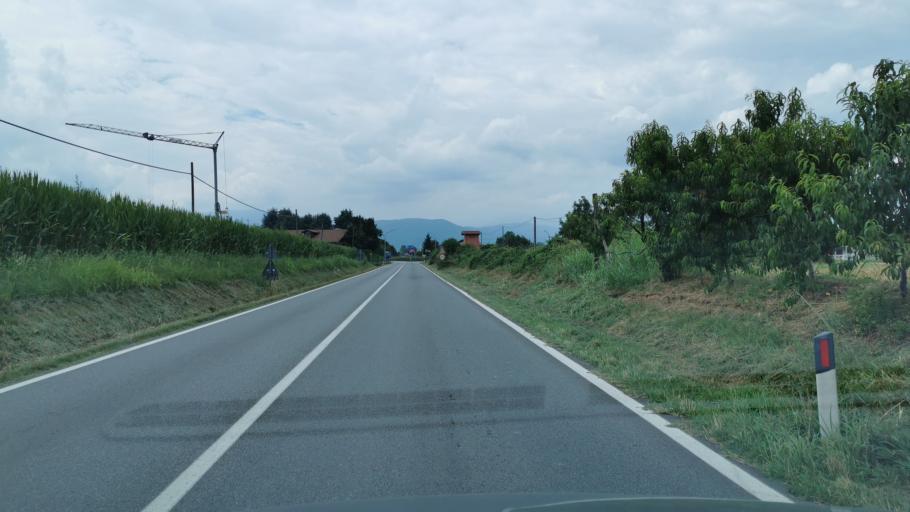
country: IT
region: Piedmont
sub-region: Provincia di Torino
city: Osasco
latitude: 44.8391
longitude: 7.3563
